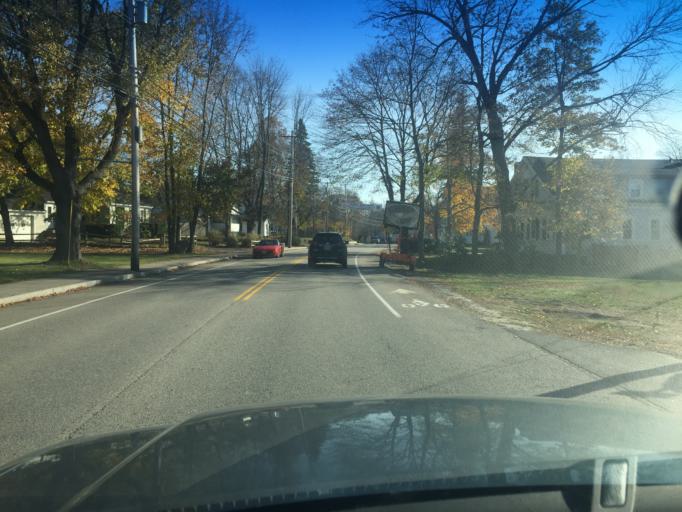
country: US
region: Maine
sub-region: York County
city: York Harbor
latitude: 43.1496
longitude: -70.6622
